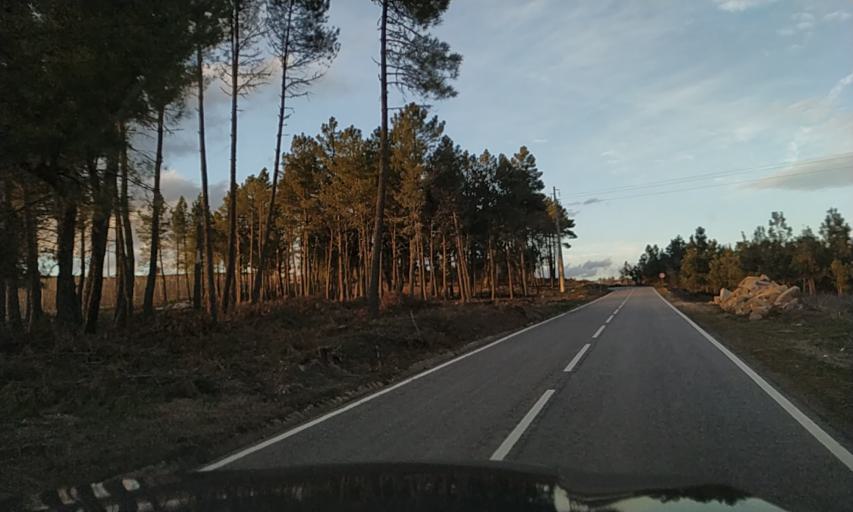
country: PT
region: Braganca
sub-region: Carrazeda de Ansiaes
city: Carrazeda de Anciaes
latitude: 41.2214
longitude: -7.3084
